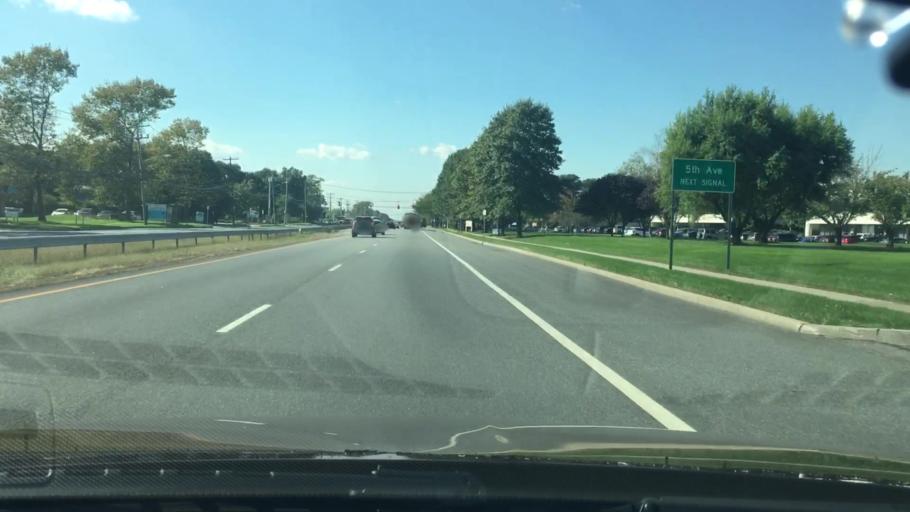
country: US
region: New York
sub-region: Suffolk County
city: Bohemia
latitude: 40.7881
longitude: -73.1353
